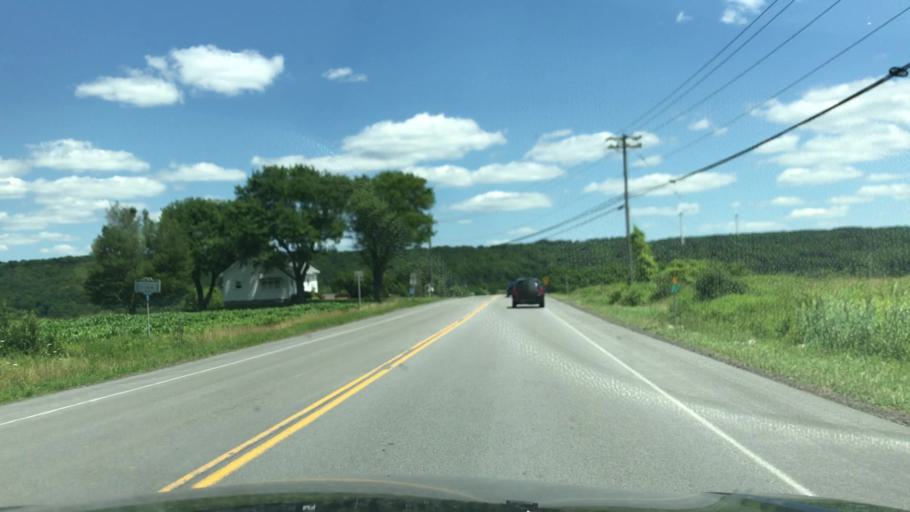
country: US
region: New York
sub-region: Wyoming County
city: Attica
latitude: 42.7704
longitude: -78.3858
